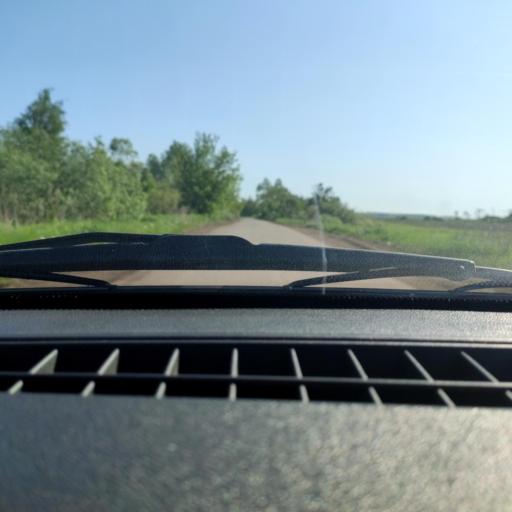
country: RU
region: Bashkortostan
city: Avdon
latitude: 54.5783
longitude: 55.8580
